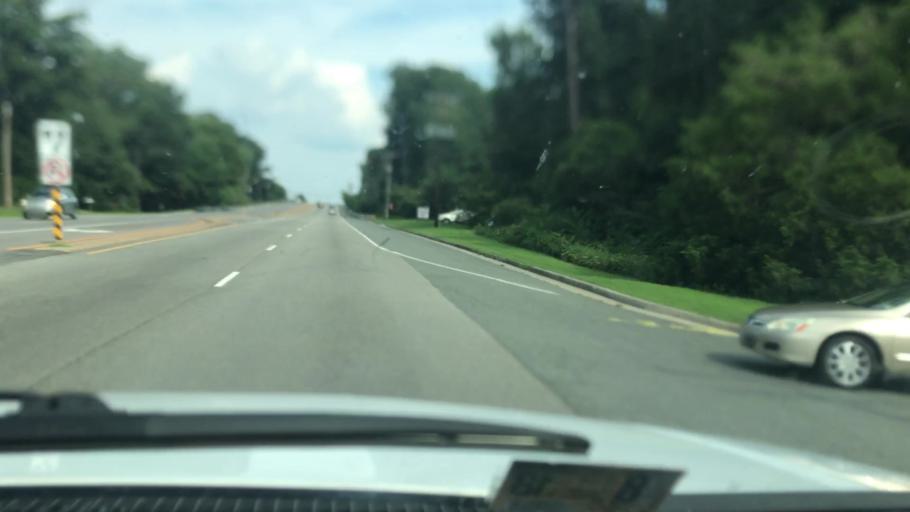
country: US
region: Virginia
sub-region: Henrico County
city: Tuckahoe
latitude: 37.5948
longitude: -77.5724
